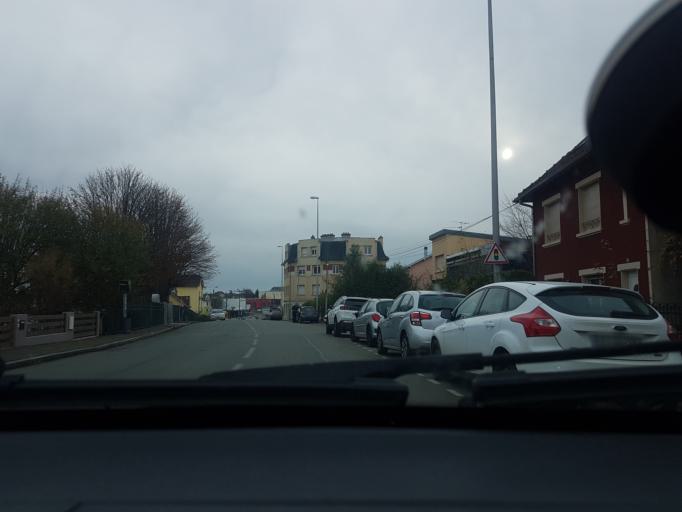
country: FR
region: Franche-Comte
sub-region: Territoire de Belfort
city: Bavilliers
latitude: 47.6288
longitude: 6.8456
